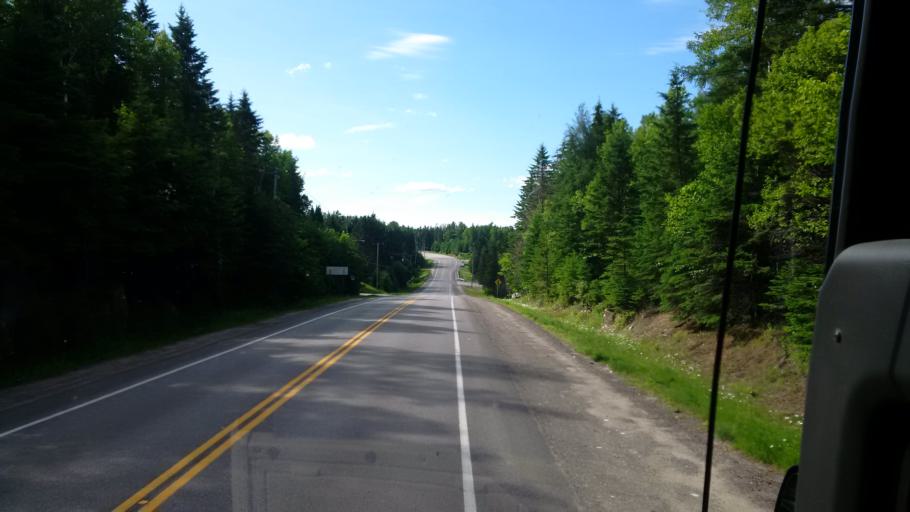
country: CA
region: Quebec
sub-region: Laurentides
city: Riviere-Rouge
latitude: 46.4313
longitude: -74.8949
